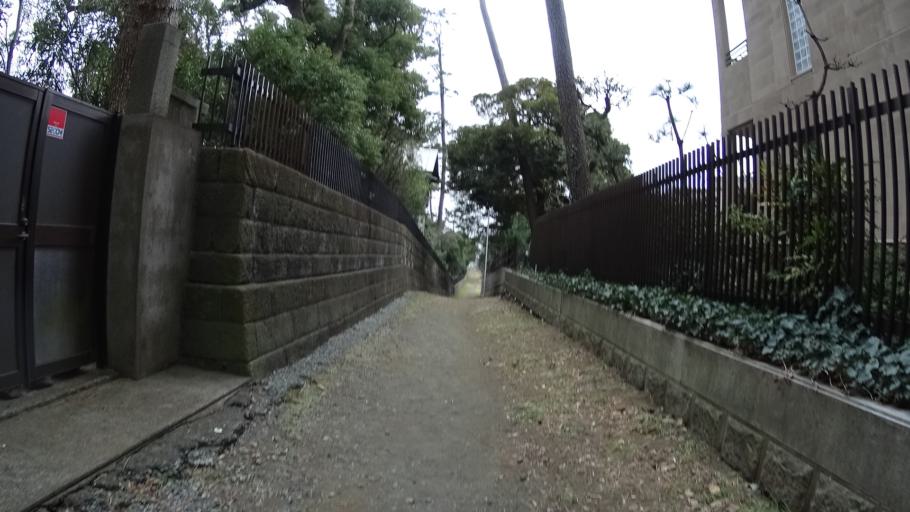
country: JP
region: Kanagawa
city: Oiso
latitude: 35.3071
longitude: 139.3053
